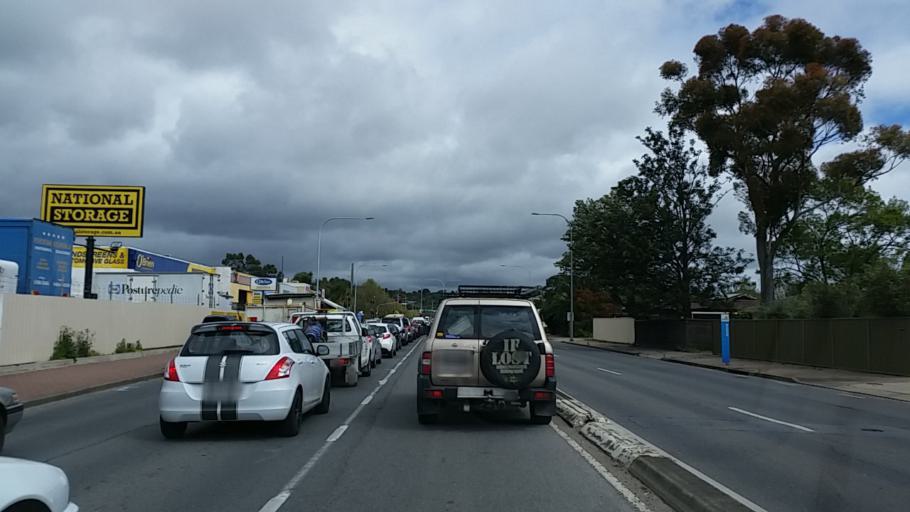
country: AU
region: South Australia
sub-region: Marion
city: Marion
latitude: -35.0153
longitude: 138.5587
